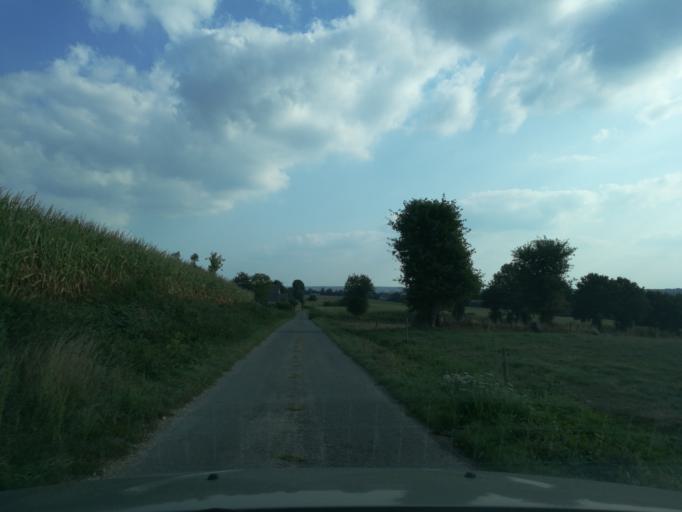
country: FR
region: Brittany
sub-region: Departement d'Ille-et-Vilaine
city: Montauban-de-Bretagne
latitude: 48.1925
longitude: -1.9968
